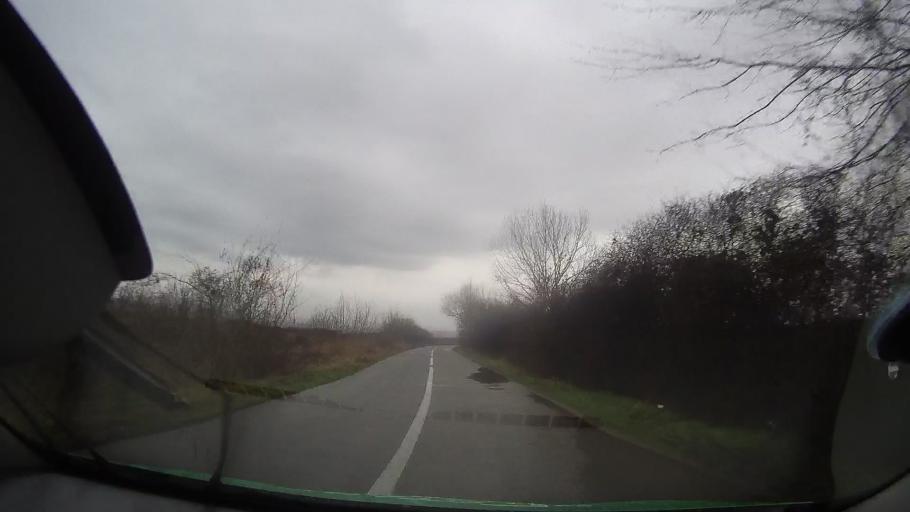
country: RO
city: Capalna
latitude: 46.7311
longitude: 22.0934
